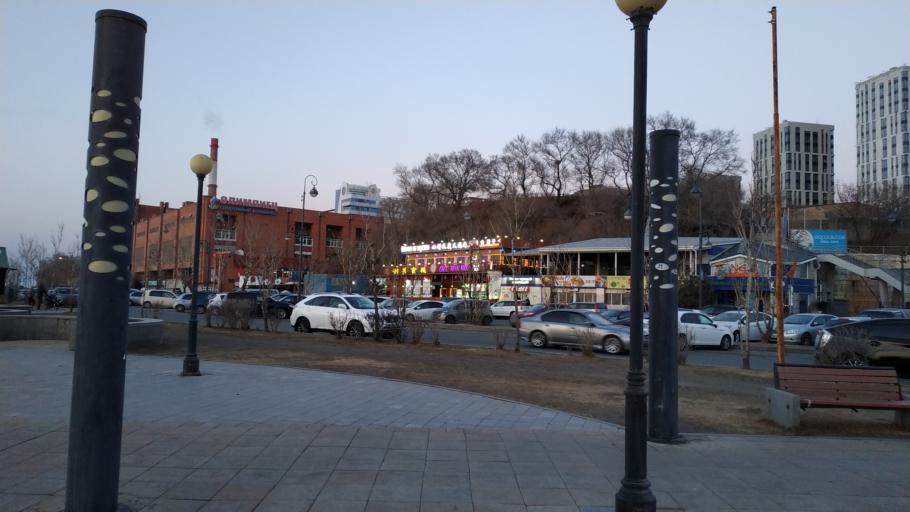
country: RU
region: Primorskiy
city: Vladivostok
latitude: 43.1215
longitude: 131.8749
